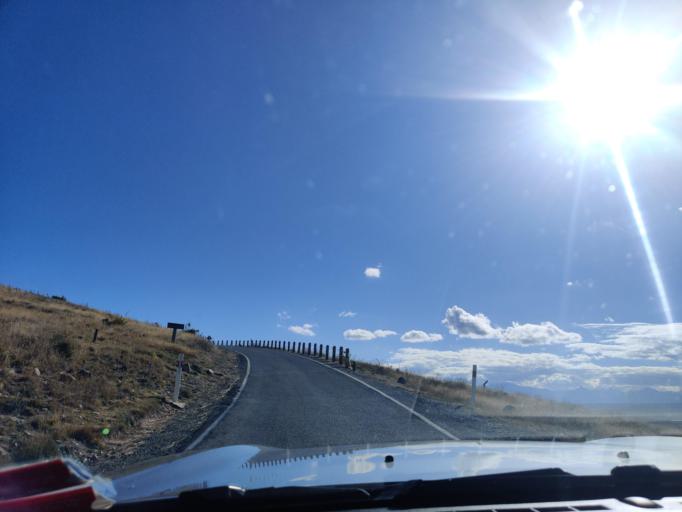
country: NZ
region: Canterbury
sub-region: Timaru District
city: Pleasant Point
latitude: -43.9841
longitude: 170.4661
